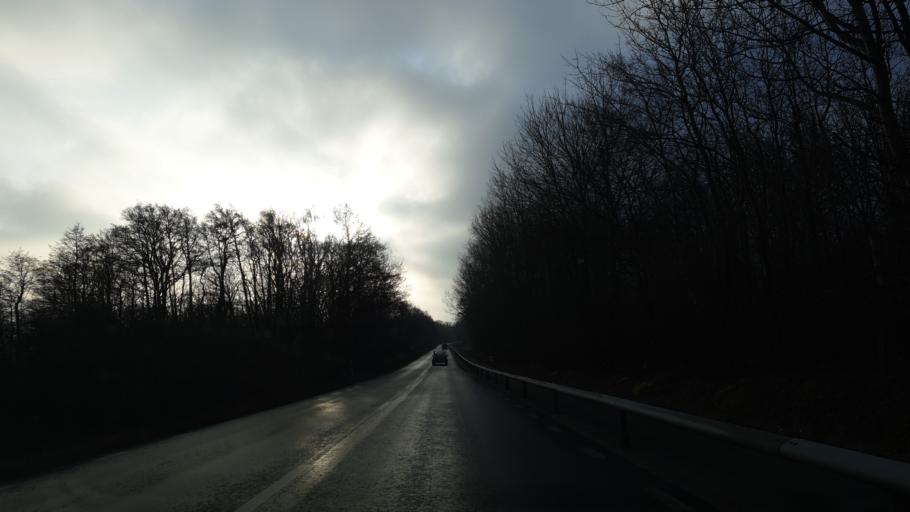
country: SE
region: Blekinge
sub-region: Karlshamns Kommun
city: Morrum
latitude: 56.1367
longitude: 14.6715
